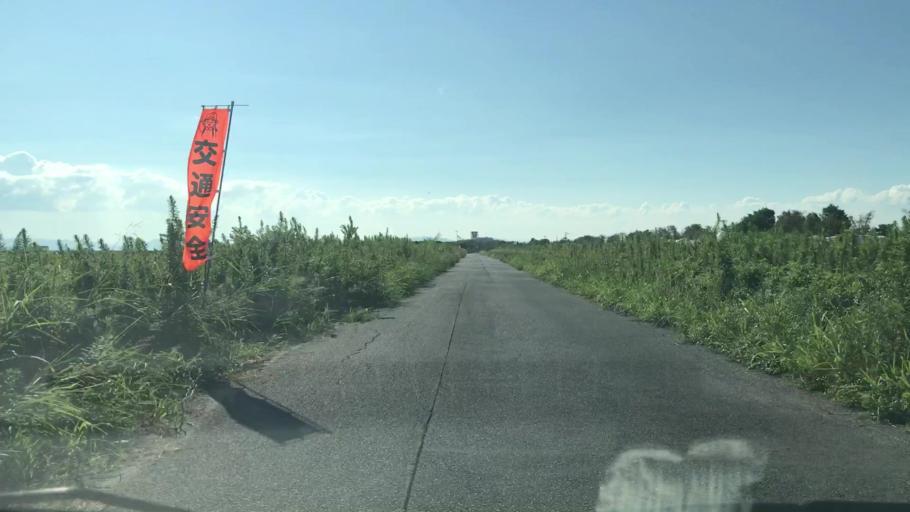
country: JP
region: Saga Prefecture
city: Okawa
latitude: 33.1514
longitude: 130.3158
